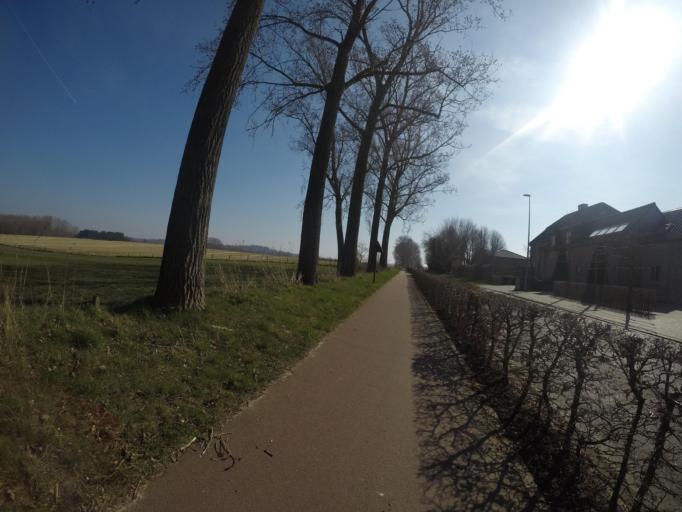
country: BE
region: Flanders
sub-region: Provincie Oost-Vlaanderen
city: Geraardsbergen
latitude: 50.7819
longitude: 3.8537
